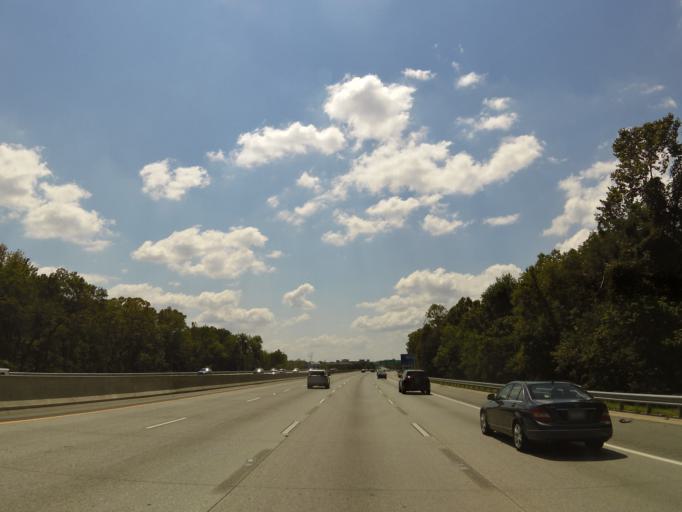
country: US
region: North Carolina
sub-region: Cabarrus County
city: Harrisburg
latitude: 35.3769
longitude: -80.7079
